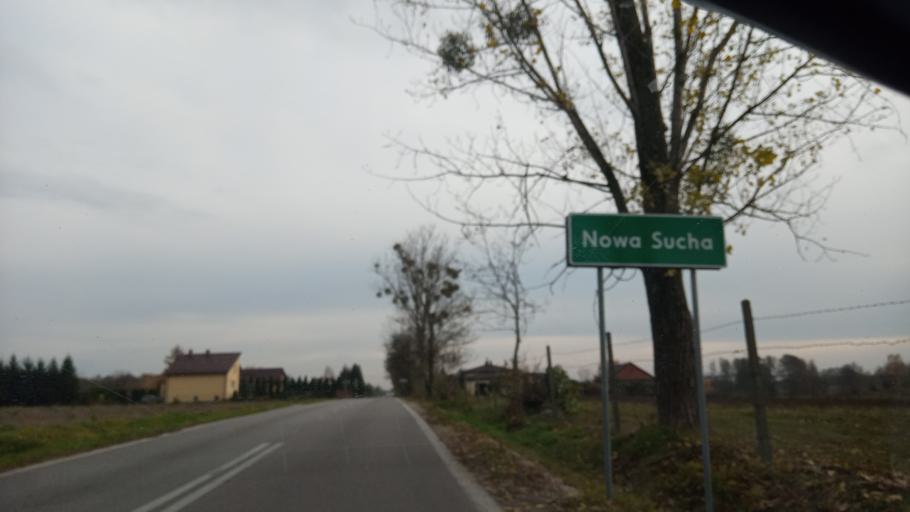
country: PL
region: Lodz Voivodeship
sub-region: Powiat skierniewicki
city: Bolimow
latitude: 52.1618
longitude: 20.1789
